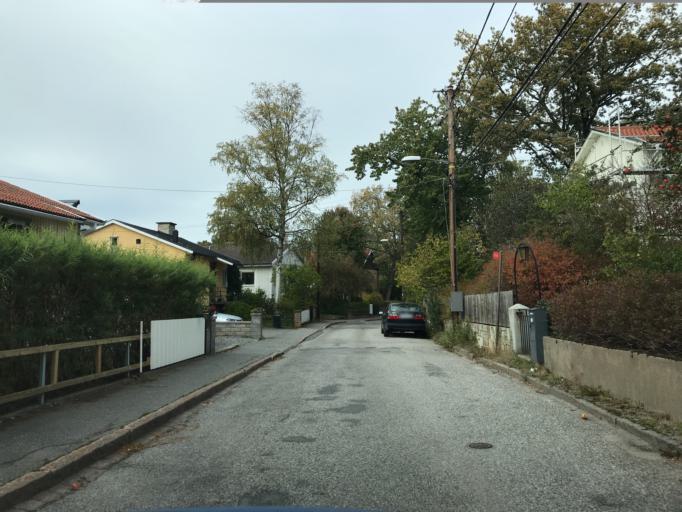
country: SE
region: Stockholm
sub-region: Huddinge Kommun
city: Segeltorp
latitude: 59.2763
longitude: 17.9656
